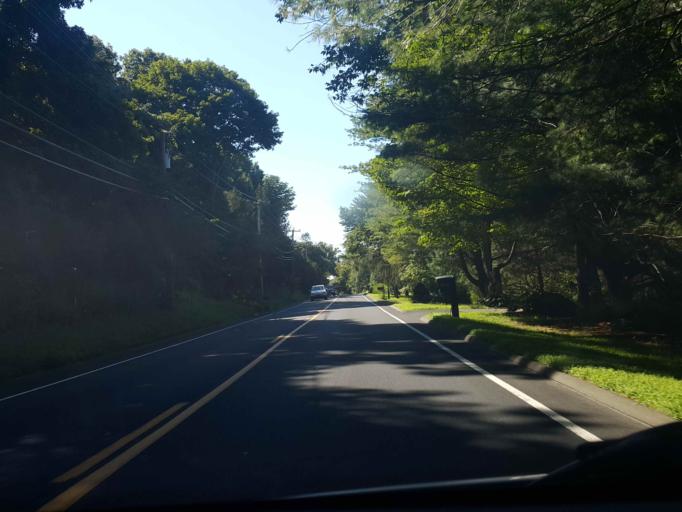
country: US
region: Connecticut
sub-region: New Haven County
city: Guilford
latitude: 41.3140
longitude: -72.6953
